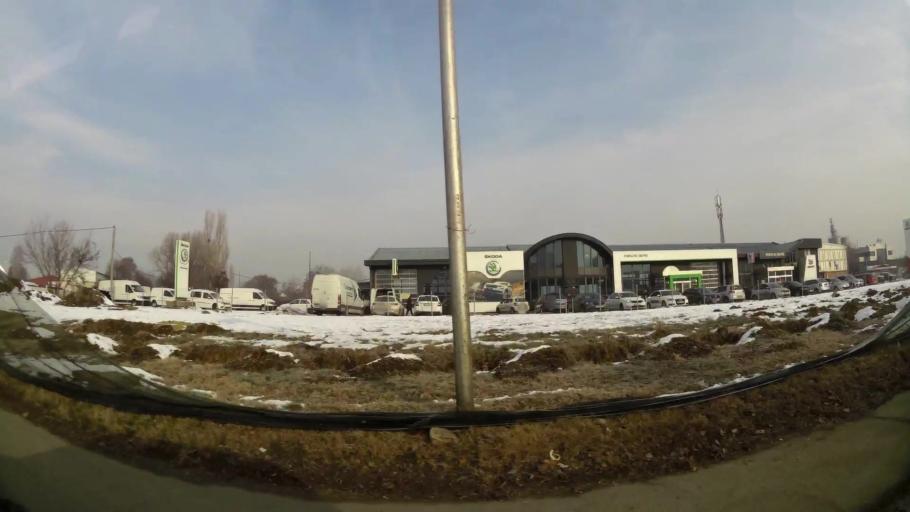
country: MK
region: Cair
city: Cair
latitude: 42.0252
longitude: 21.4348
